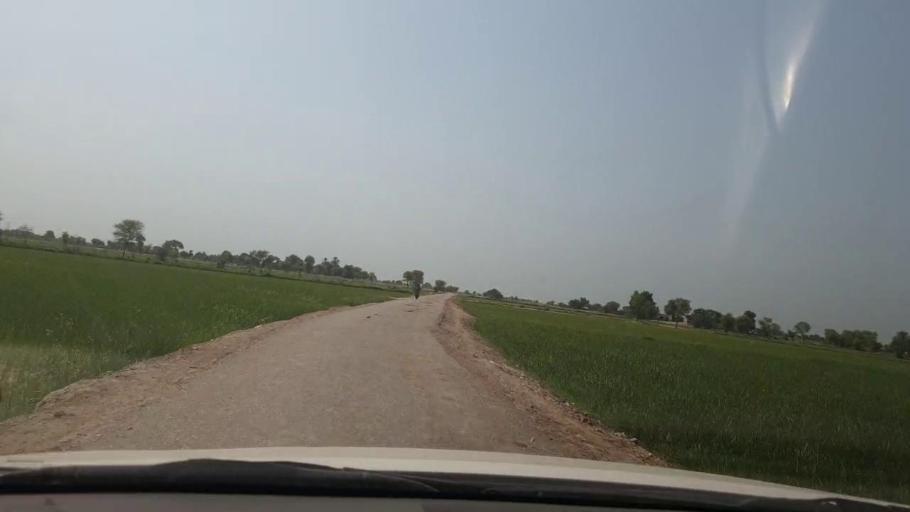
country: PK
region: Sindh
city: Shikarpur
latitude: 28.0045
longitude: 68.7155
